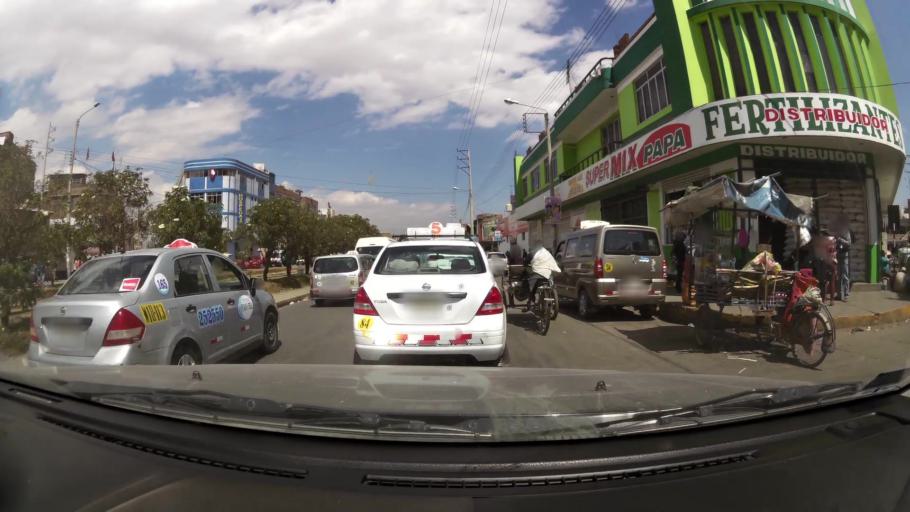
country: PE
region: Junin
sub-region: Provincia de Huancayo
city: Huancayo
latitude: -12.0726
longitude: -75.2048
